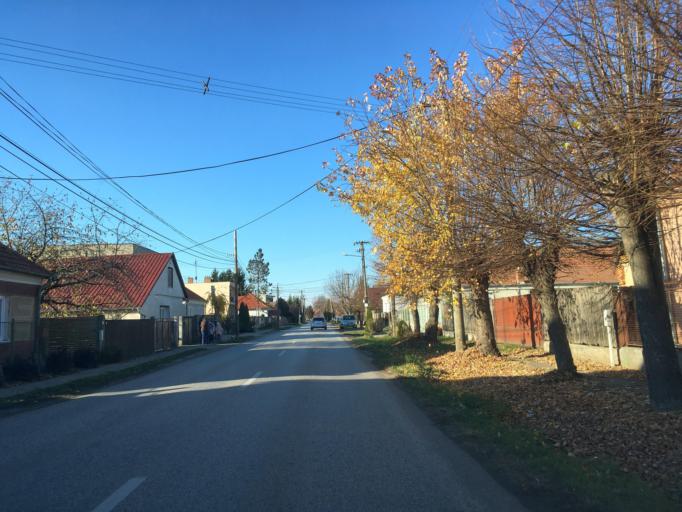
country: SK
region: Nitriansky
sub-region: Okres Nove Zamky
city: Nove Zamky
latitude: 47.9210
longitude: 18.1321
